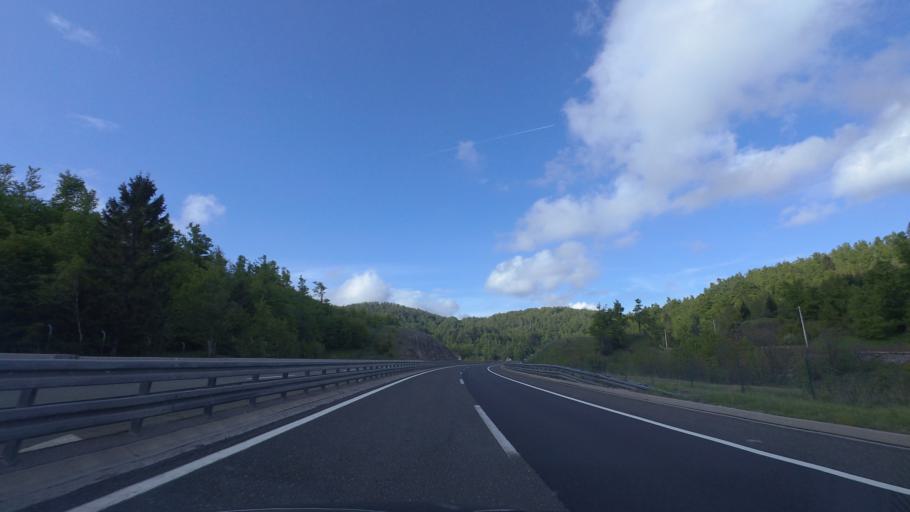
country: HR
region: Primorsko-Goranska
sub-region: Grad Delnice
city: Delnice
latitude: 45.3359
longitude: 14.7393
